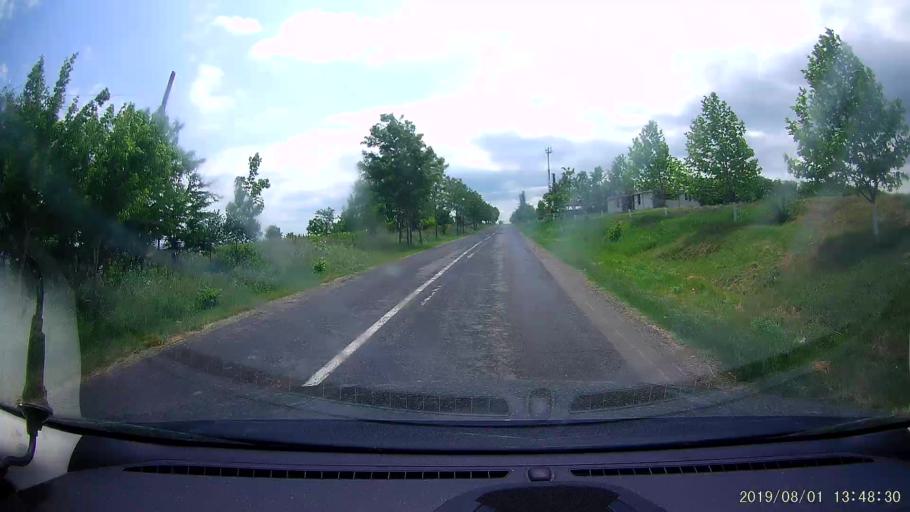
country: RO
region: Galati
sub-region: Comuna Oancea
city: Oancea
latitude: 45.9073
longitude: 28.1119
